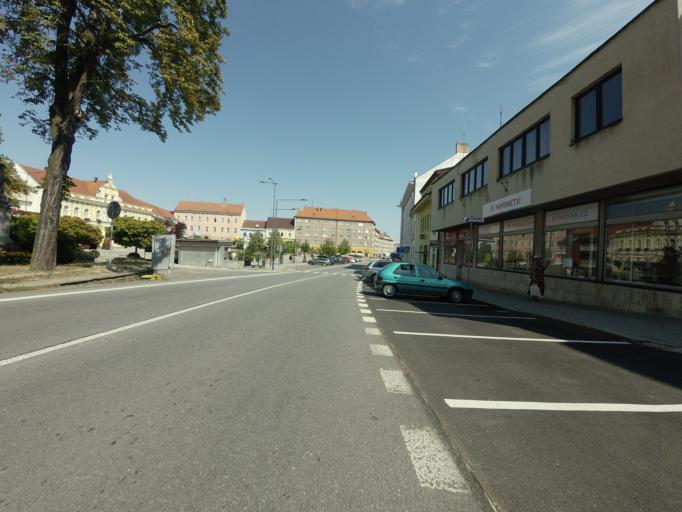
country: CZ
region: Jihocesky
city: Milevsko
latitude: 49.4497
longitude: 14.3596
